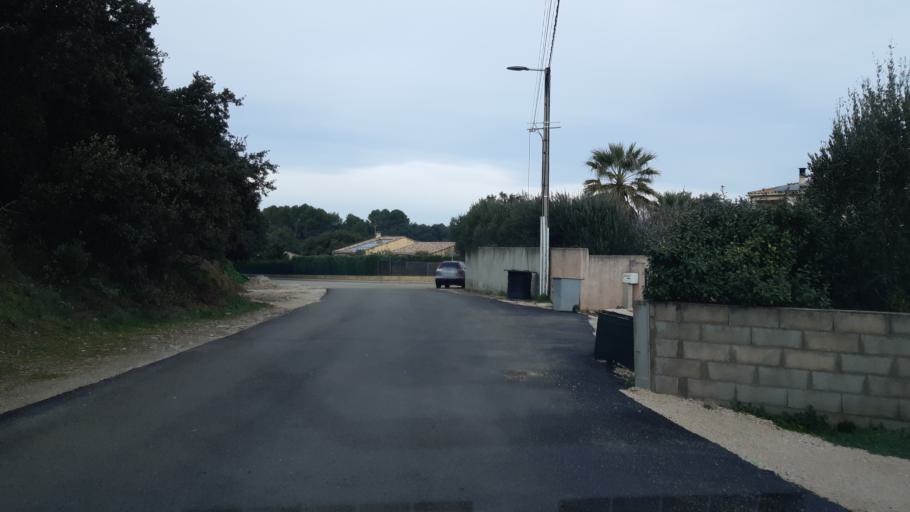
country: FR
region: Languedoc-Roussillon
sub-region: Departement du Gard
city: Comps
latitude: 43.8432
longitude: 4.6035
